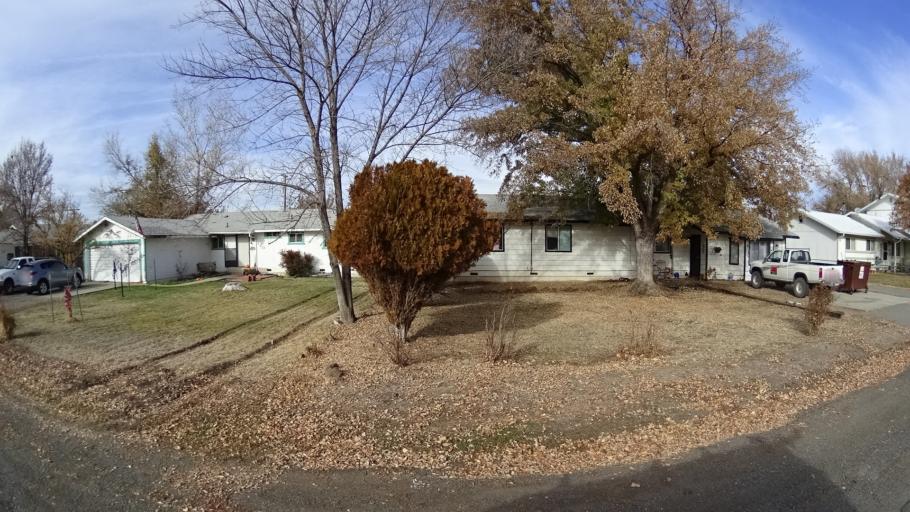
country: US
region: California
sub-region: Siskiyou County
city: Montague
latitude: 41.7257
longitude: -122.5190
